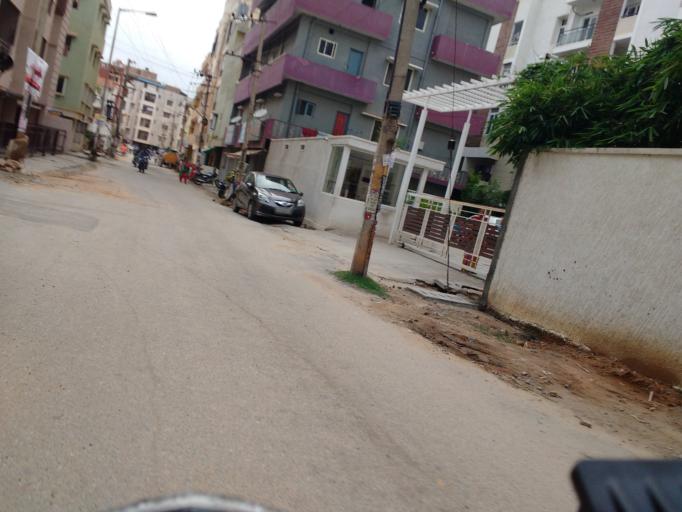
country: IN
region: Karnataka
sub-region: Bangalore Urban
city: Bangalore
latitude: 12.9909
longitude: 77.6699
